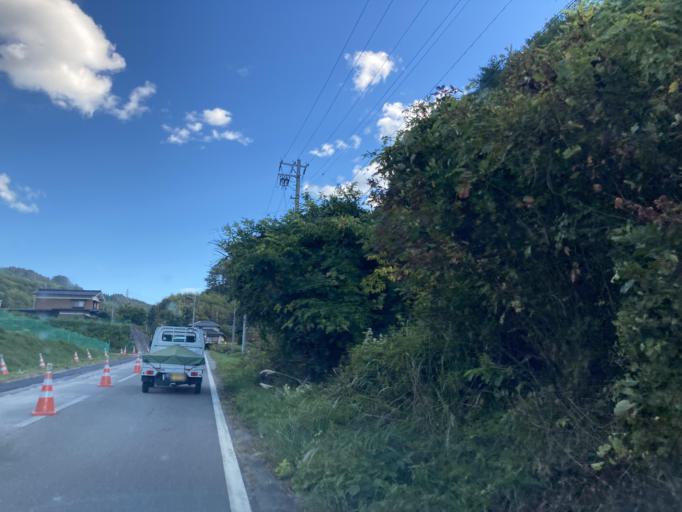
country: JP
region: Nagano
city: Ueda
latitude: 36.4171
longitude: 138.1032
